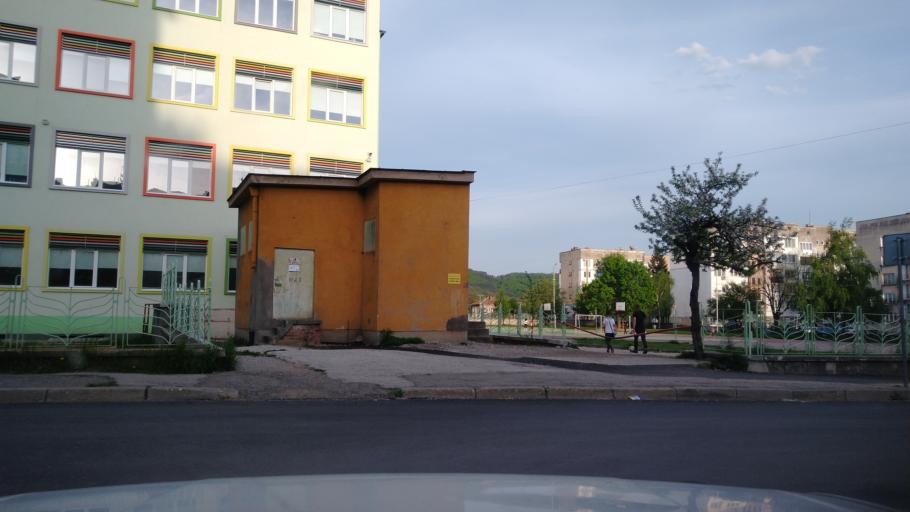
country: BG
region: Gabrovo
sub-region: Obshtina Gabrovo
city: Gabrovo
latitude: 42.8892
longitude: 25.3119
